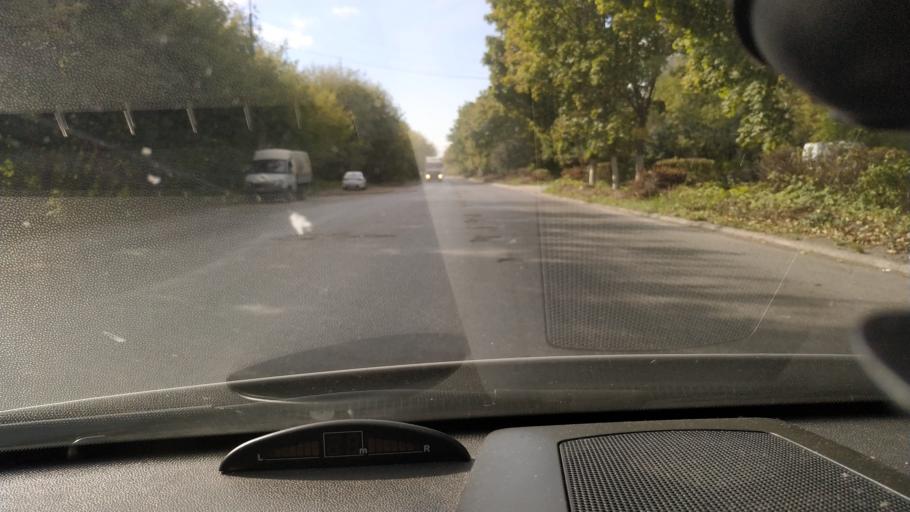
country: RU
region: Rjazan
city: Ryazan'
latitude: 54.6493
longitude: 39.6548
